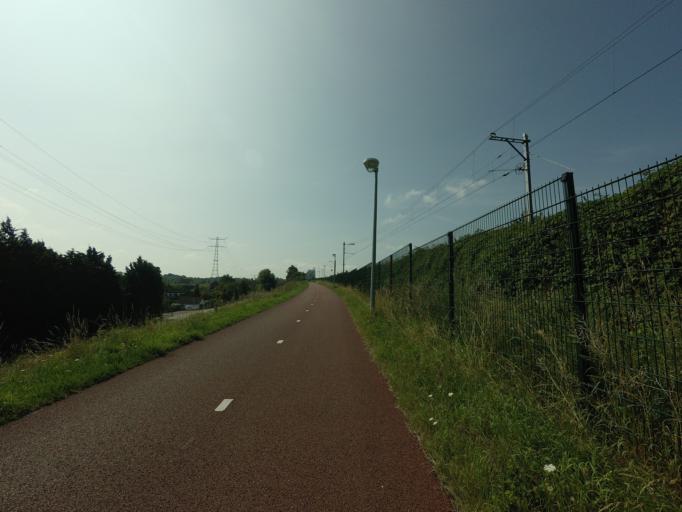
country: NL
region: South Holland
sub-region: Gemeente Sliedrecht
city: Sliedrecht
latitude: 51.8259
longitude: 4.7418
